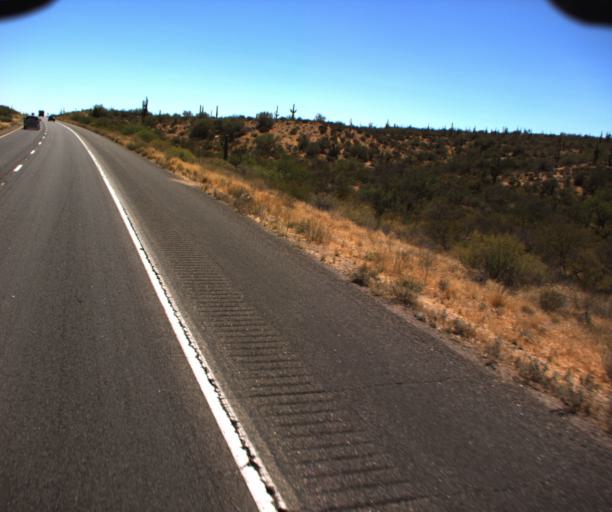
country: US
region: Arizona
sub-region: Maricopa County
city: Rio Verde
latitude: 33.6710
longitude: -111.5108
